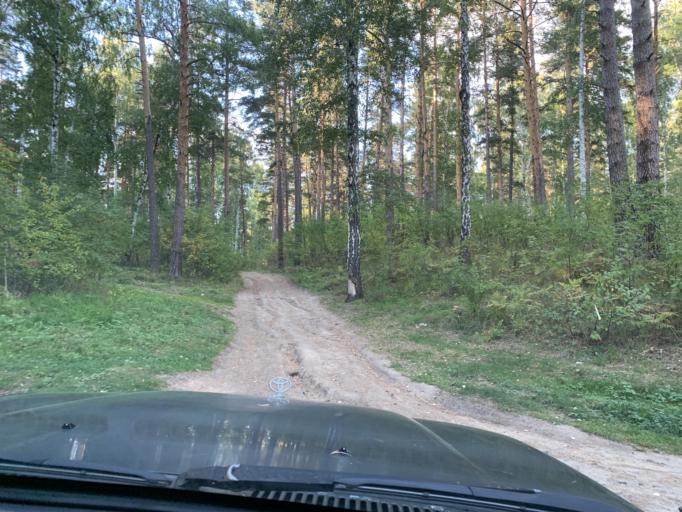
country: RU
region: Chelyabinsk
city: Vishnevogorsk
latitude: 55.9980
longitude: 60.5064
